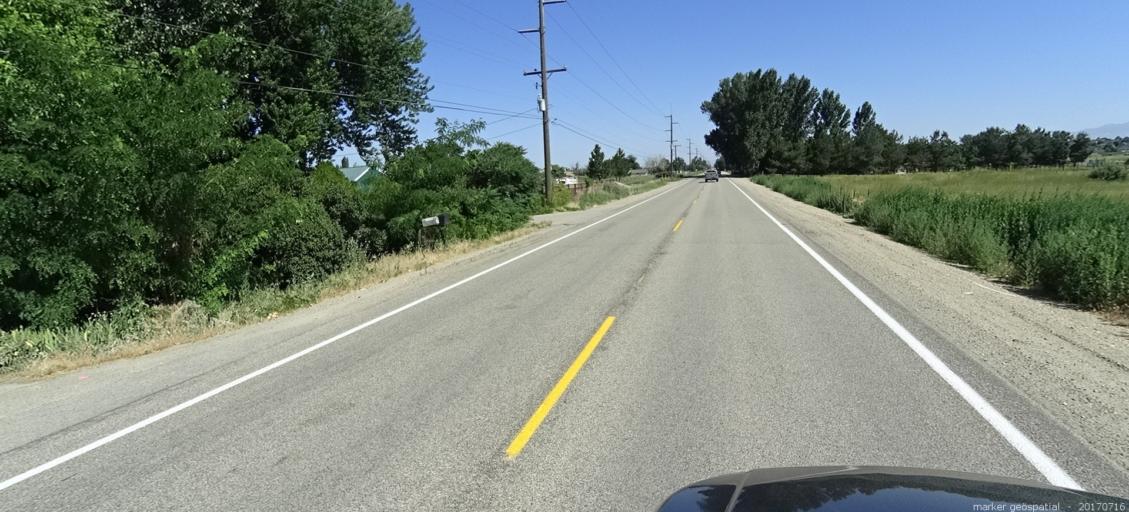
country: US
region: Idaho
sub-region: Ada County
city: Kuna
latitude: 43.5214
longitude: -116.3345
